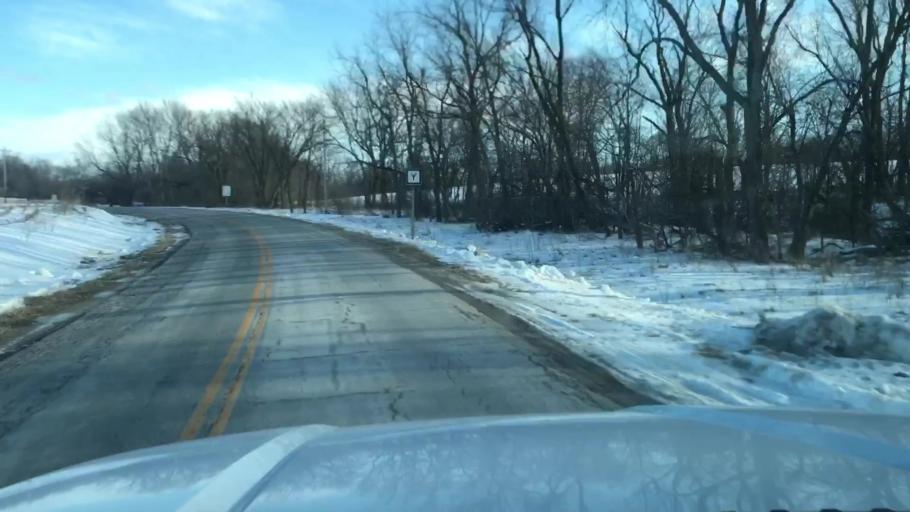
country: US
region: Missouri
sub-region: Holt County
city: Oregon
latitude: 40.1015
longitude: -95.0214
